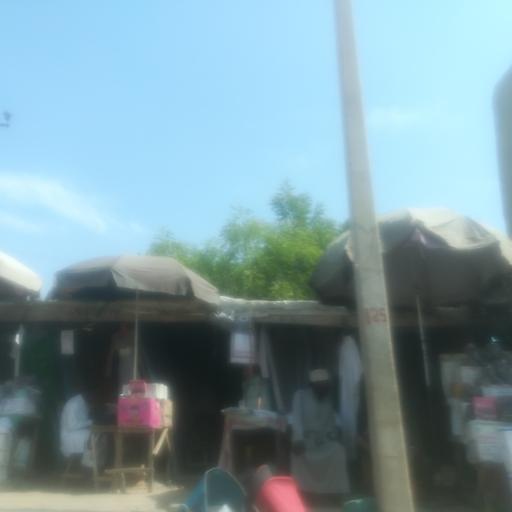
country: NG
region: Kano
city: Kano
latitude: 12.0250
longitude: 8.5217
